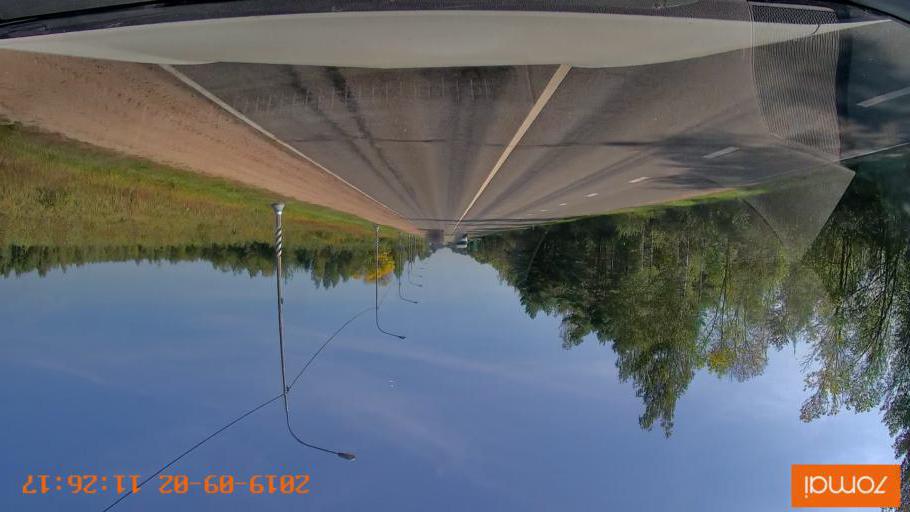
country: RU
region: Smolensk
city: Roslavl'
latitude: 53.9936
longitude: 32.9340
